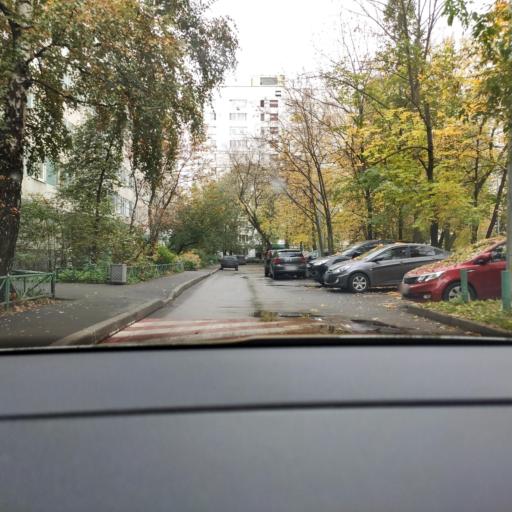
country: RU
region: Moscow
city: Yaroslavskiy
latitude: 55.8737
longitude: 37.7106
